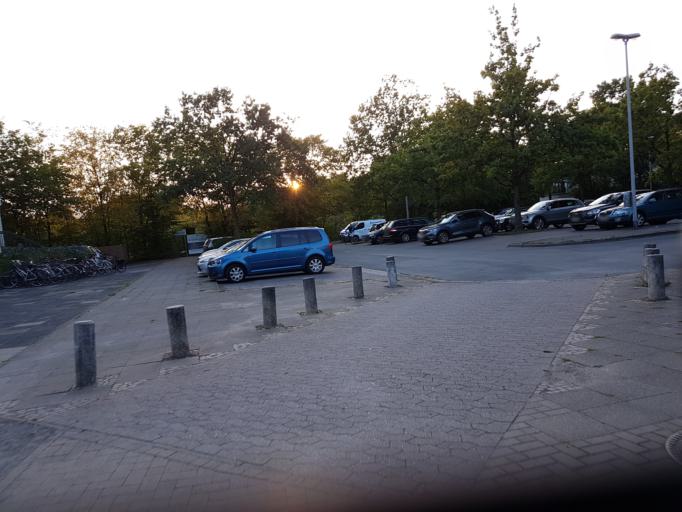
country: DE
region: Lower Saxony
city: Langenhagen
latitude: 52.4208
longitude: 9.7944
